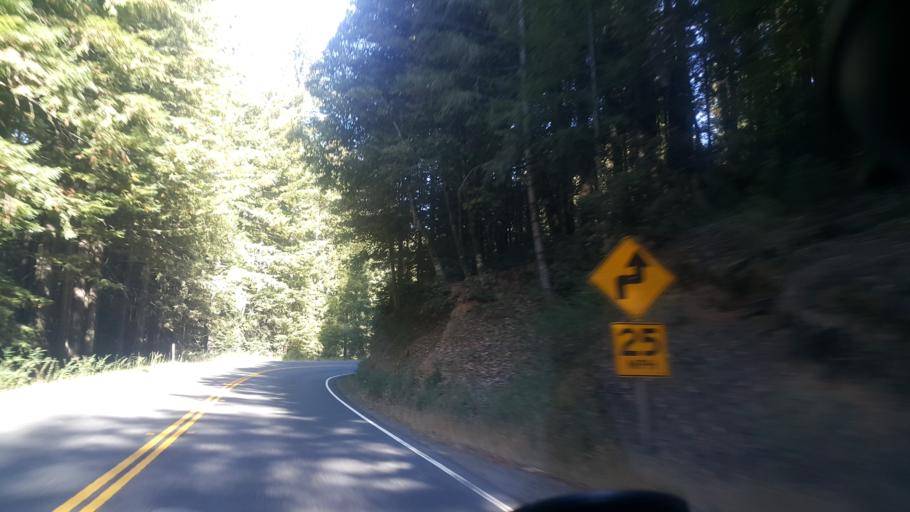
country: US
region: California
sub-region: Mendocino County
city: Fort Bragg
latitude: 39.3637
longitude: -123.6706
